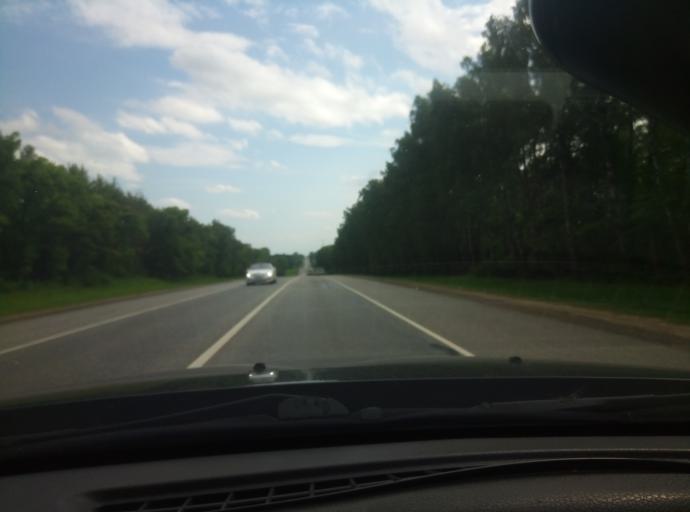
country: RU
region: Tula
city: Leninskiy
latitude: 54.3645
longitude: 37.5283
